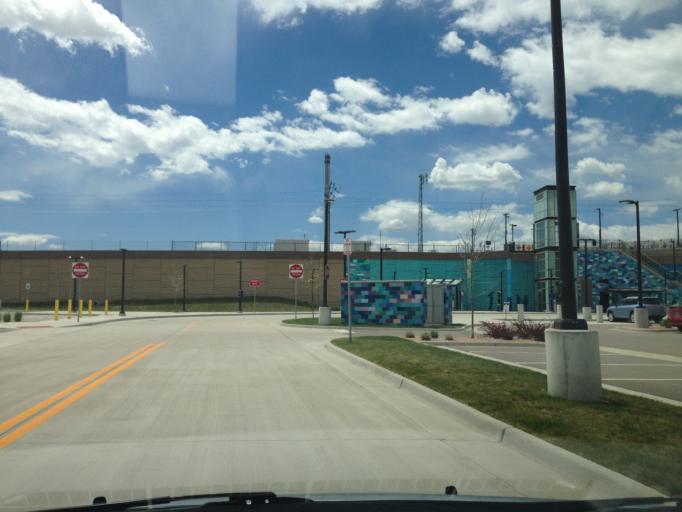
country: US
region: Colorado
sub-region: Adams County
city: Berkley
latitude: 39.8046
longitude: -105.0224
